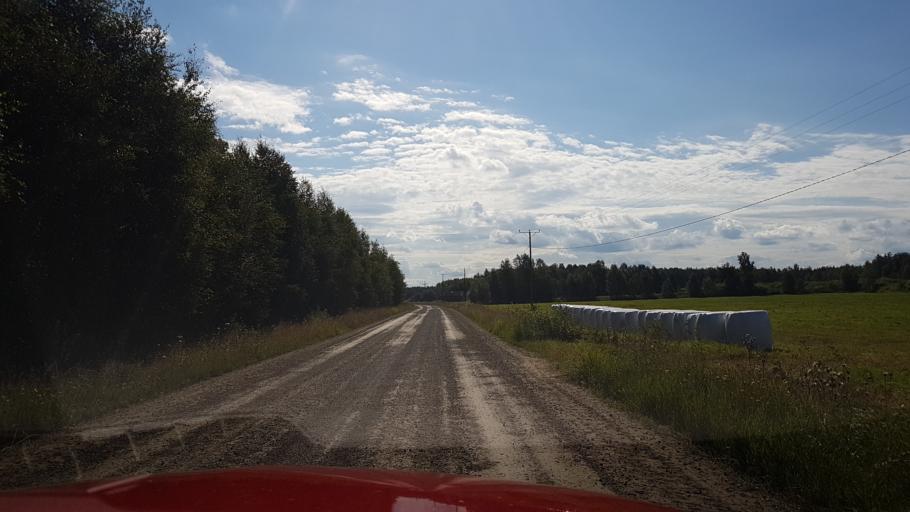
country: FI
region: Northern Ostrobothnia
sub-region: Ylivieska
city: Himanka
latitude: 64.0695
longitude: 23.8218
